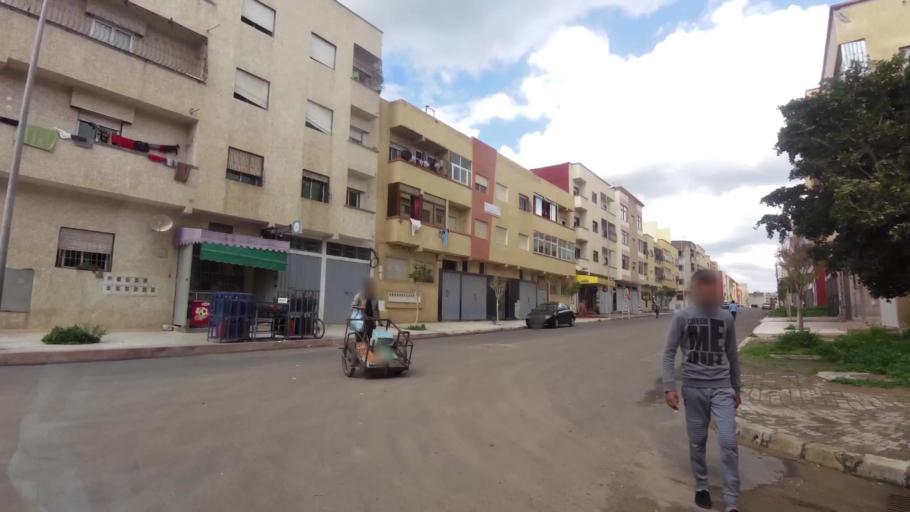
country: MA
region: Chaouia-Ouardigha
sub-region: Settat Province
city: Berrechid
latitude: 33.2737
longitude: -7.5915
